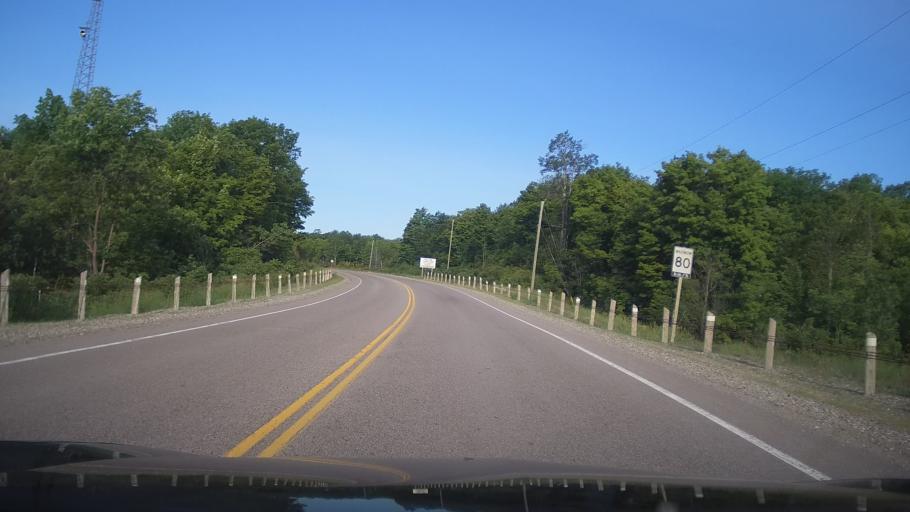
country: CA
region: Ontario
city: Perth
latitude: 44.7948
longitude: -76.6977
